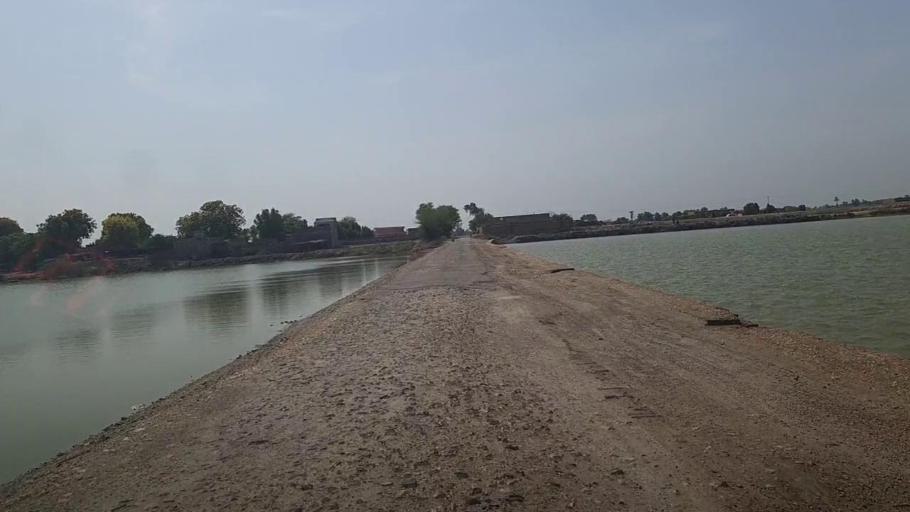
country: PK
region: Sindh
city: Ubauro
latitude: 28.1364
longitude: 69.8263
